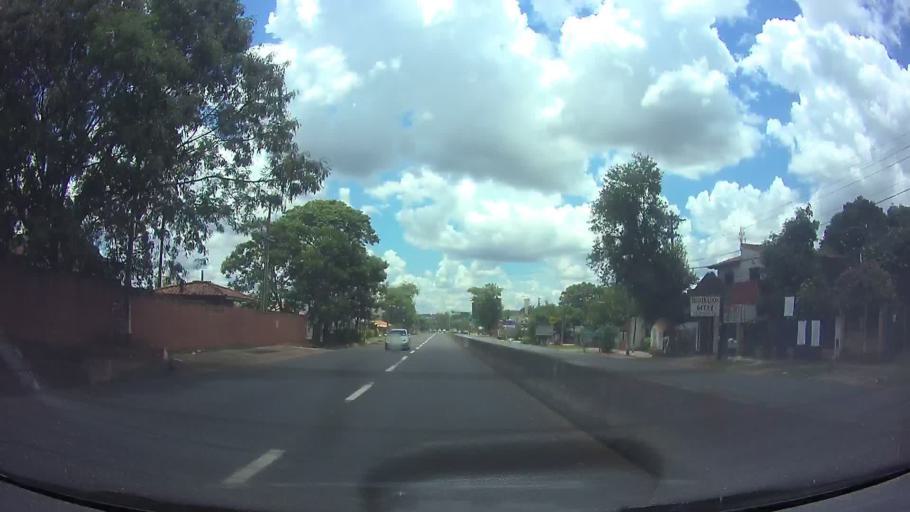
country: PY
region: Central
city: Capiata
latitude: -25.3641
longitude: -57.4260
